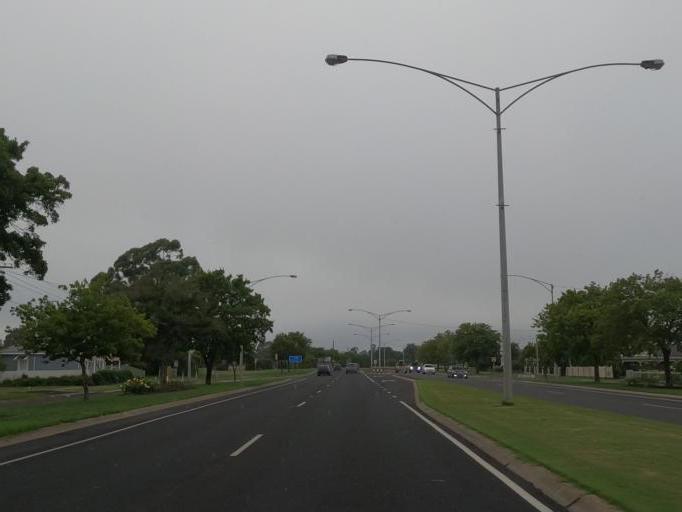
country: AU
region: Victoria
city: Brown Hill
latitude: -37.5584
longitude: 143.8866
